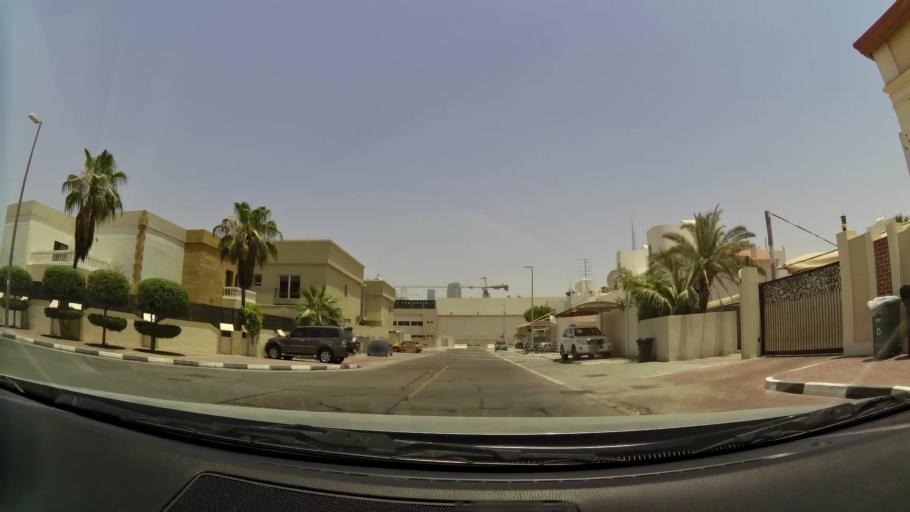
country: AE
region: Dubai
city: Dubai
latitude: 25.2188
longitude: 55.2579
